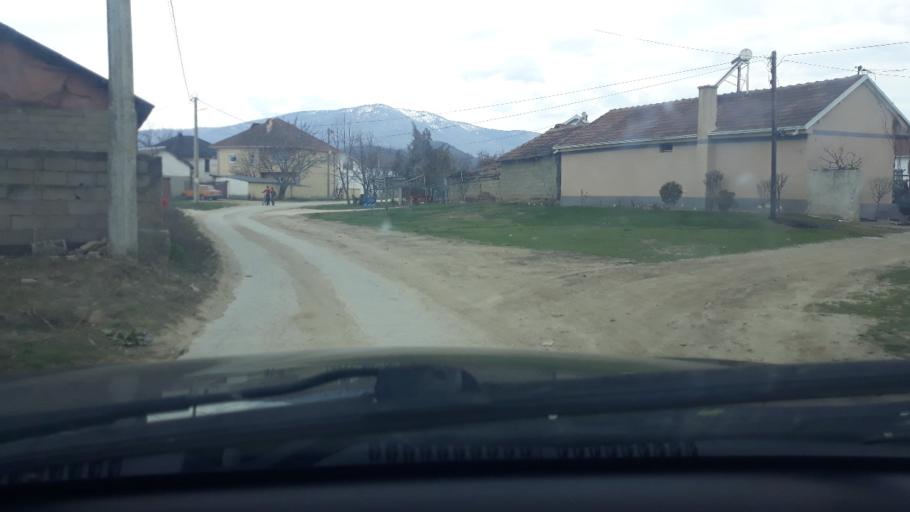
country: MK
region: Krivogastani
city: Obrsani
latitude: 41.2819
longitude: 21.3396
